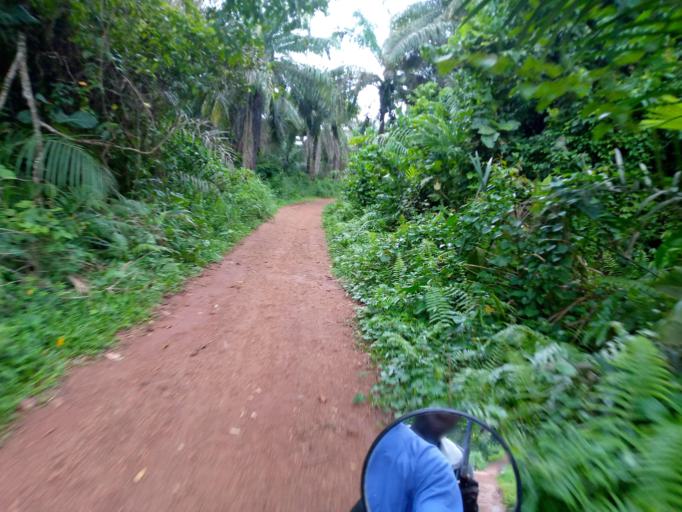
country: SL
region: Northern Province
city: Mange
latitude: 8.9862
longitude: -12.7150
